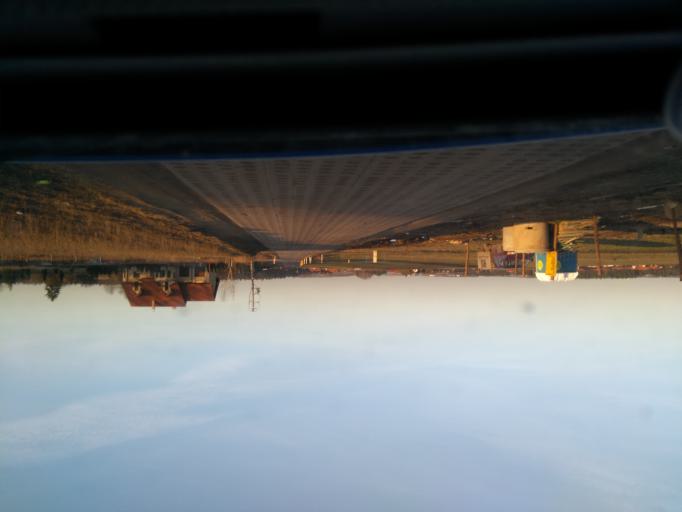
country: PL
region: Pomeranian Voivodeship
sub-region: Powiat kartuski
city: Banino
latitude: 54.3820
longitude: 18.3966
